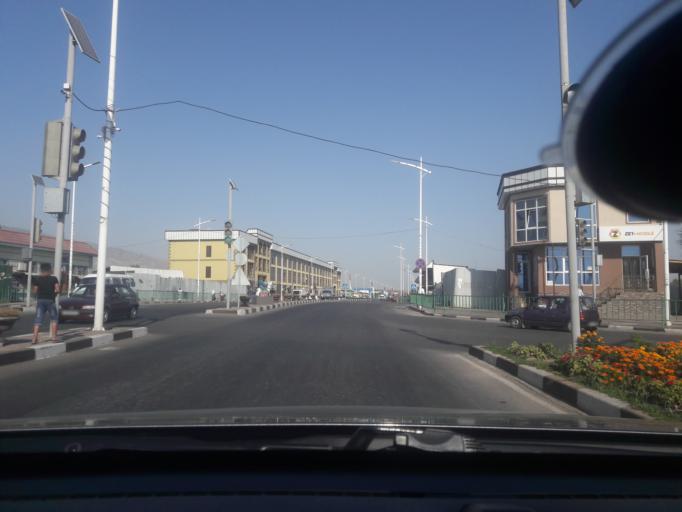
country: TJ
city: Shahrinav
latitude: 38.5767
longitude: 68.3301
